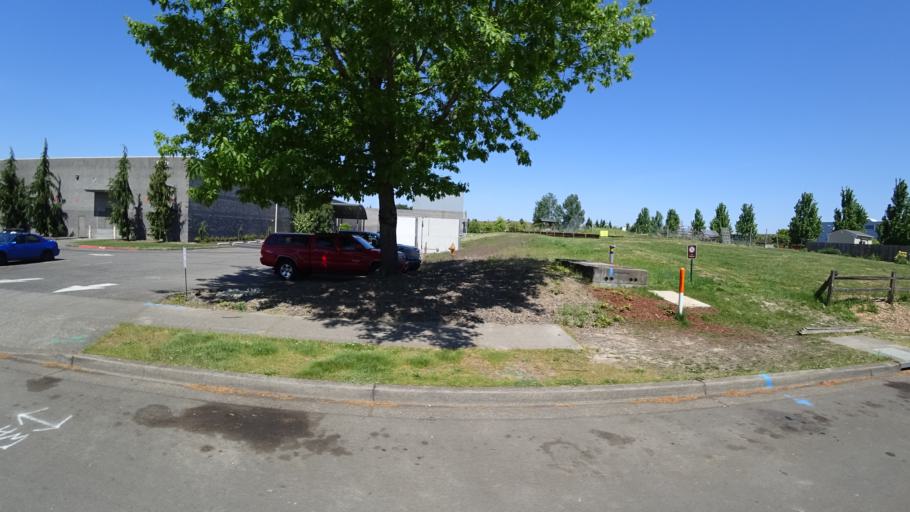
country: US
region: Oregon
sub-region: Washington County
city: Rockcreek
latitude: 45.5322
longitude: -122.9104
